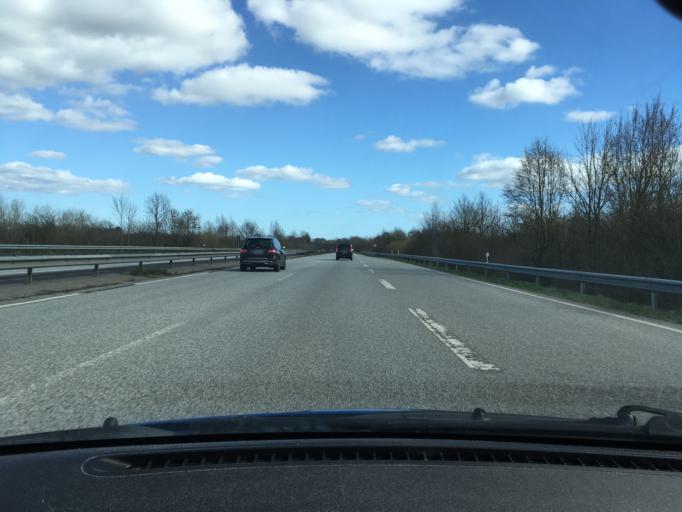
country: DE
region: Schleswig-Holstein
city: Bredenbek
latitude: 54.3167
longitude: 9.8605
